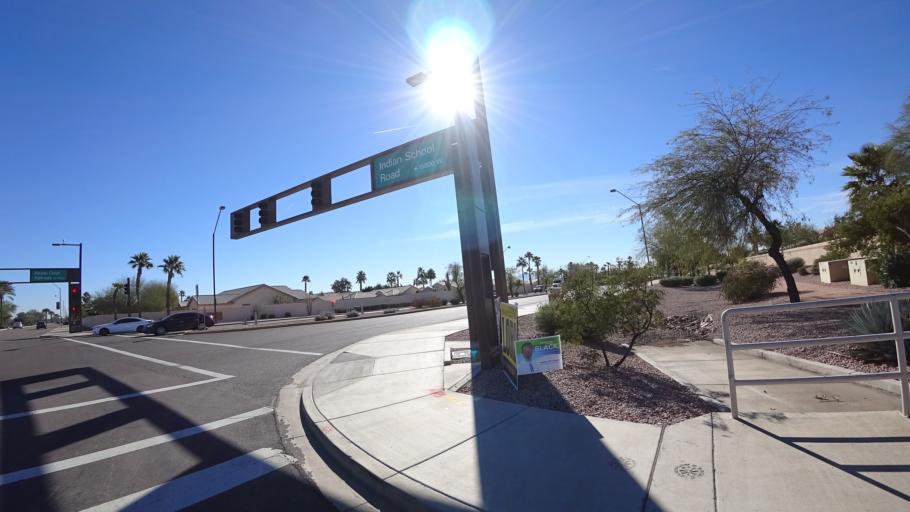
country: US
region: Arizona
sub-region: Maricopa County
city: Litchfield Park
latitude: 33.4935
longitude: -112.4014
